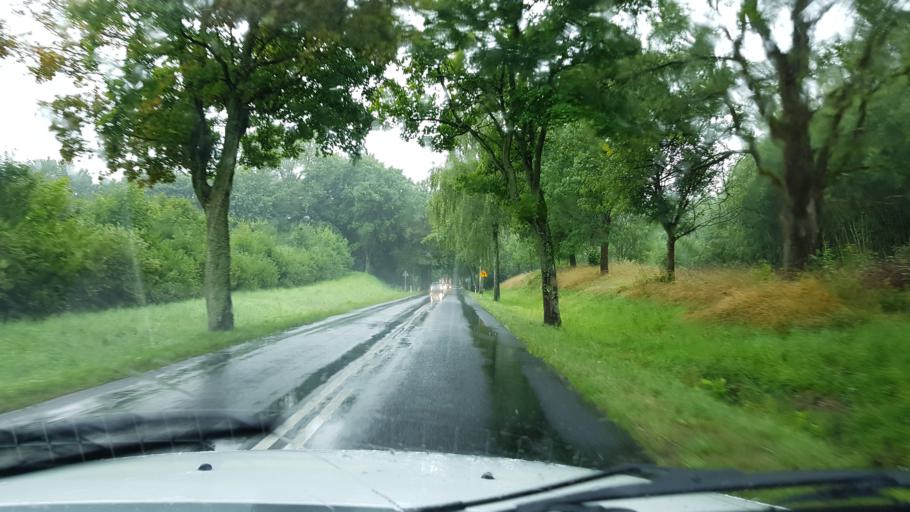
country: PL
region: West Pomeranian Voivodeship
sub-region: Powiat goleniowski
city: Nowogard
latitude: 53.5971
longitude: 15.1543
